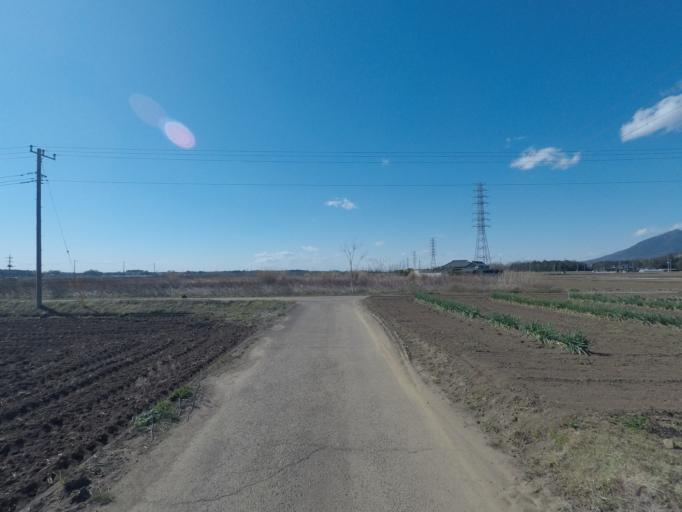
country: JP
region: Ibaraki
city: Tsukuba
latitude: 36.1378
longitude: 140.1160
